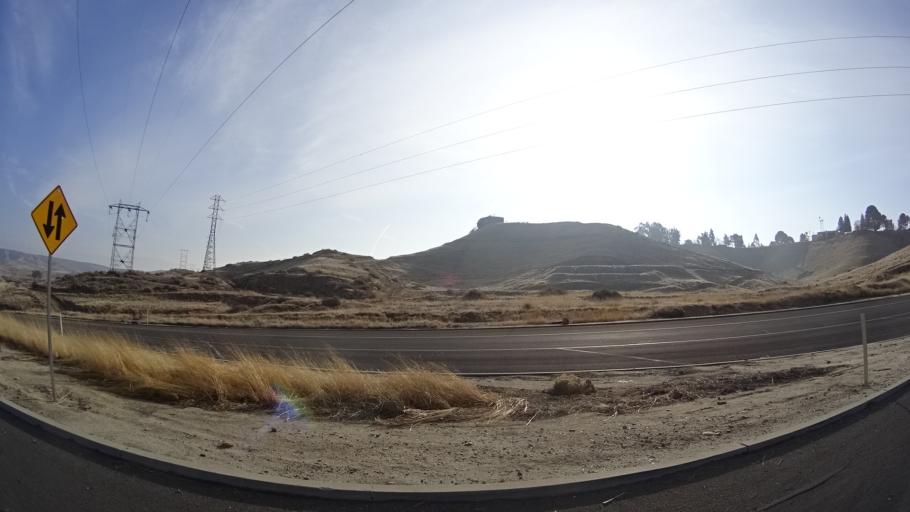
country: US
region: California
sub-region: Kern County
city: Oildale
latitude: 35.4166
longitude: -118.9598
